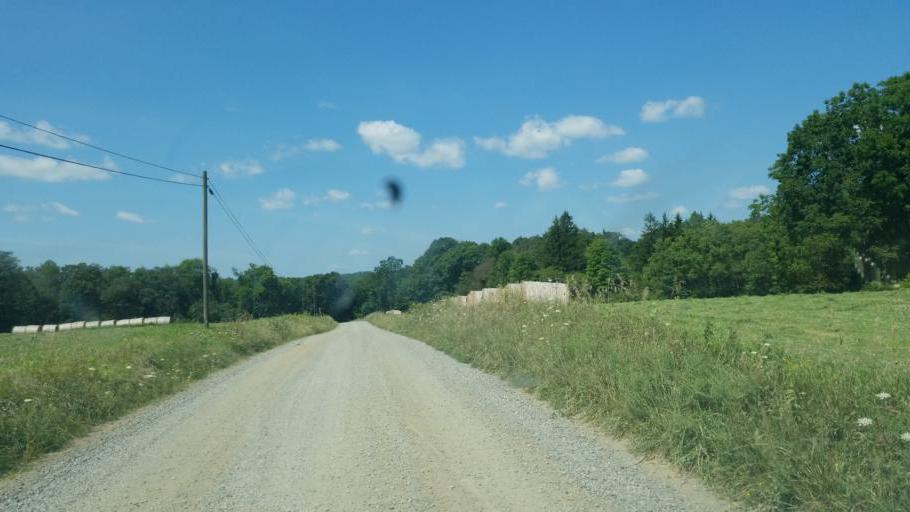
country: US
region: Pennsylvania
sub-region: Clarion County
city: Knox
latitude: 41.2009
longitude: -79.5572
